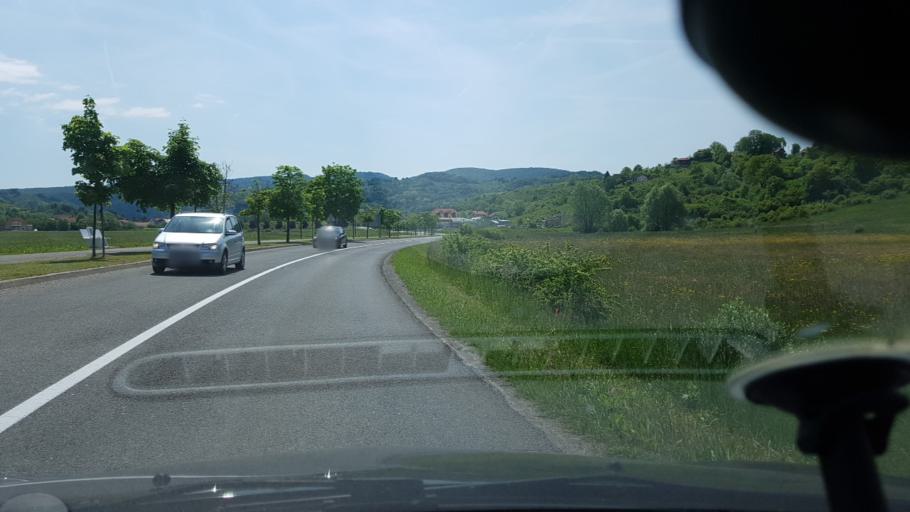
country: HR
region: Krapinsko-Zagorska
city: Marija Bistrica
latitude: 46.0043
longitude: 16.1104
